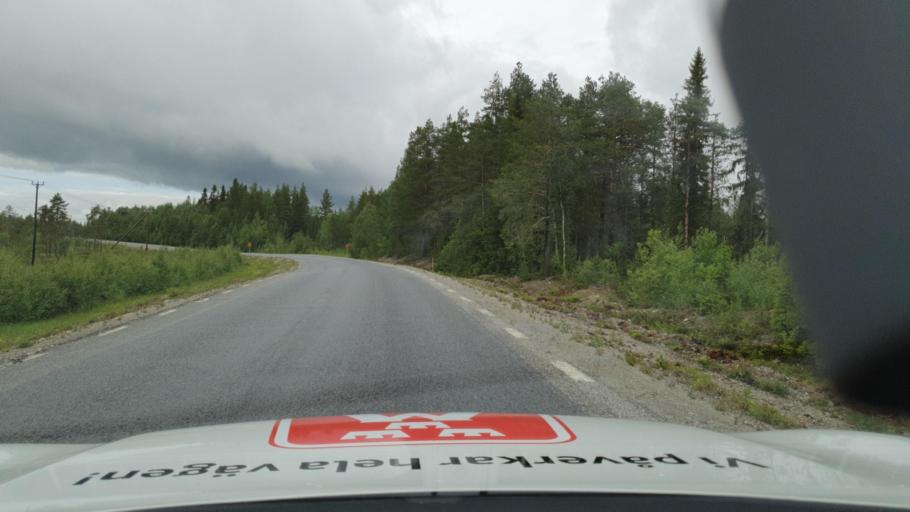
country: SE
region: Vaesterbotten
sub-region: Dorotea Kommun
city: Dorotea
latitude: 64.1852
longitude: 16.6235
